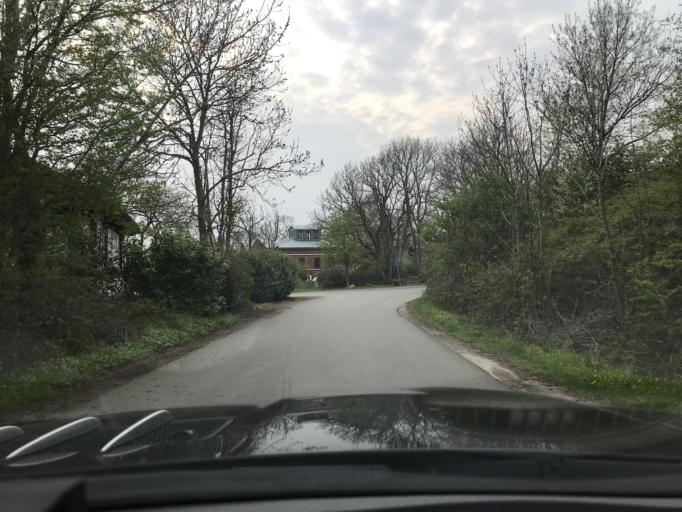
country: DE
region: Schleswig-Holstein
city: Burg auf Fehmarn
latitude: 54.4143
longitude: 11.2769
